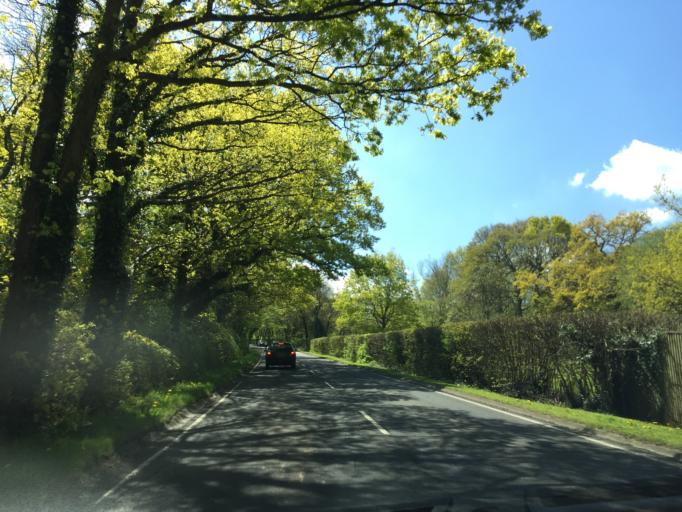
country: GB
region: England
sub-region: Kent
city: Edenbridge
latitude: 51.1348
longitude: 0.1070
